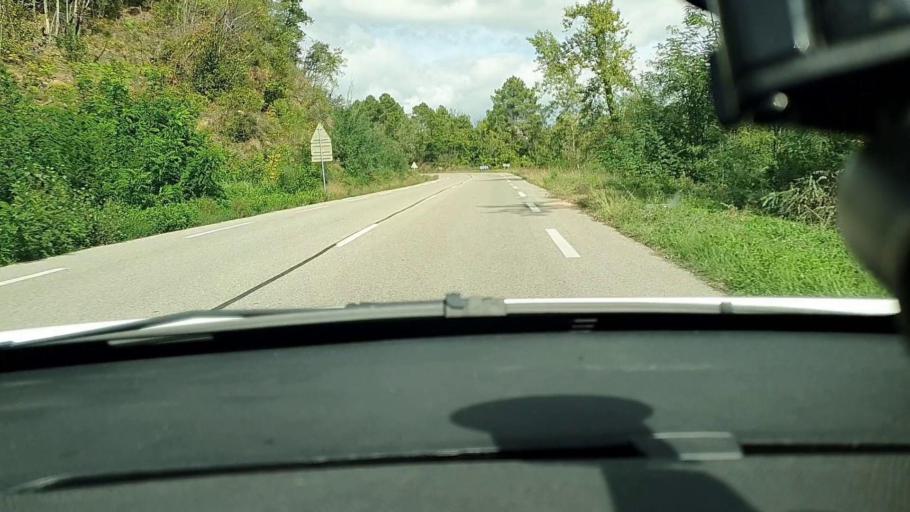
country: FR
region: Languedoc-Roussillon
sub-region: Departement du Gard
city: Laval-Pradel
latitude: 44.2295
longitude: 4.0537
